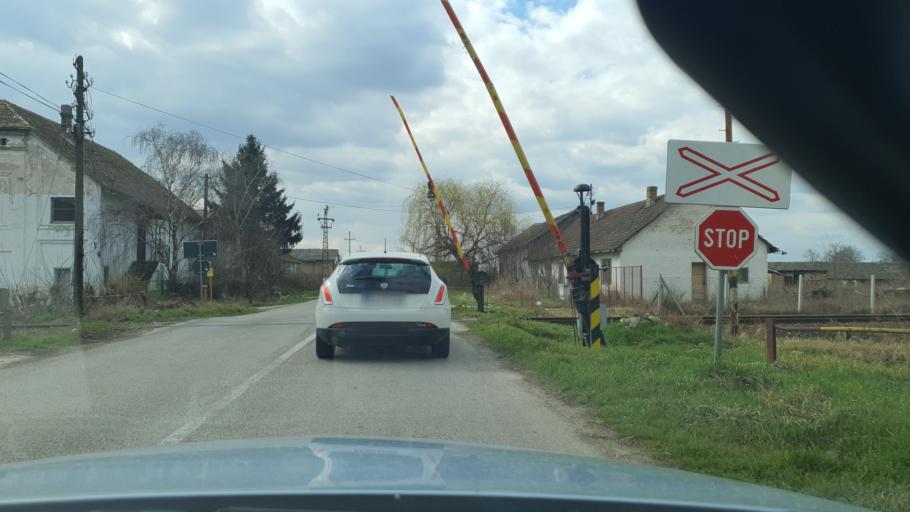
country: RS
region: Autonomna Pokrajina Vojvodina
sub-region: Zapadnobacki Okrug
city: Odzaci
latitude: 45.4475
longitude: 19.3284
